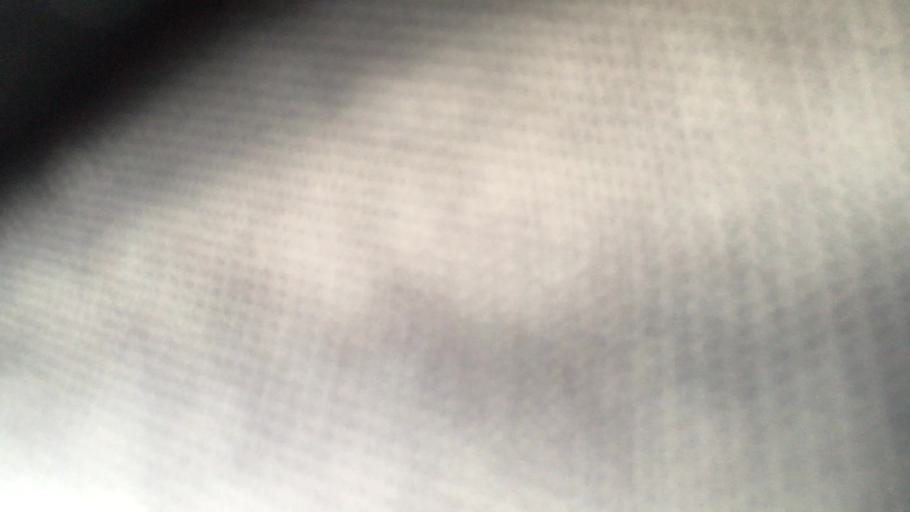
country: US
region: Maryland
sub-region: Somerset County
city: Princess Anne
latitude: 38.1791
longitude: -75.6897
